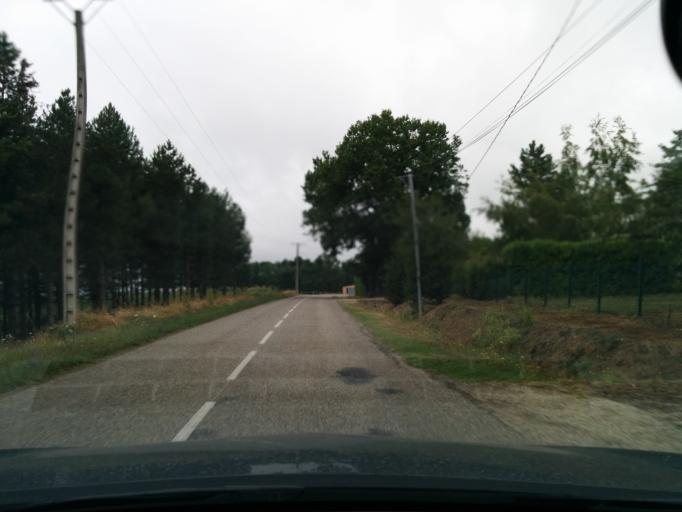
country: FR
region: Midi-Pyrenees
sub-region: Departement du Tarn-et-Garonne
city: Moissac
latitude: 44.1543
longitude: 1.0649
